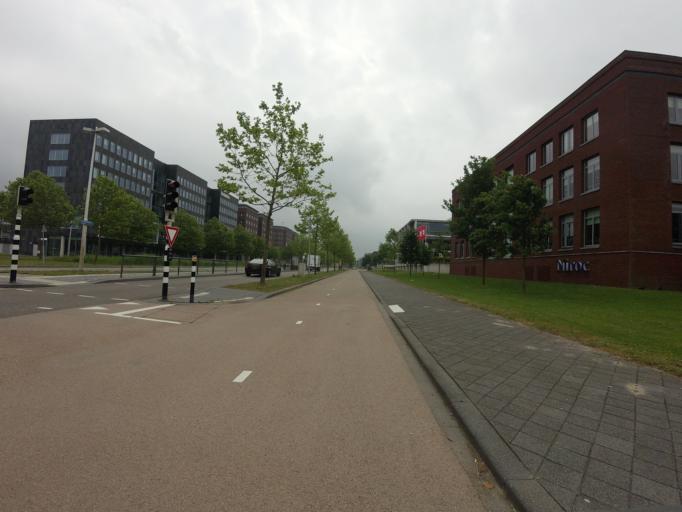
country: NL
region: Utrecht
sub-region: Gemeente Nieuwegein
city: Nieuwegein
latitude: 52.0683
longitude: 5.0812
